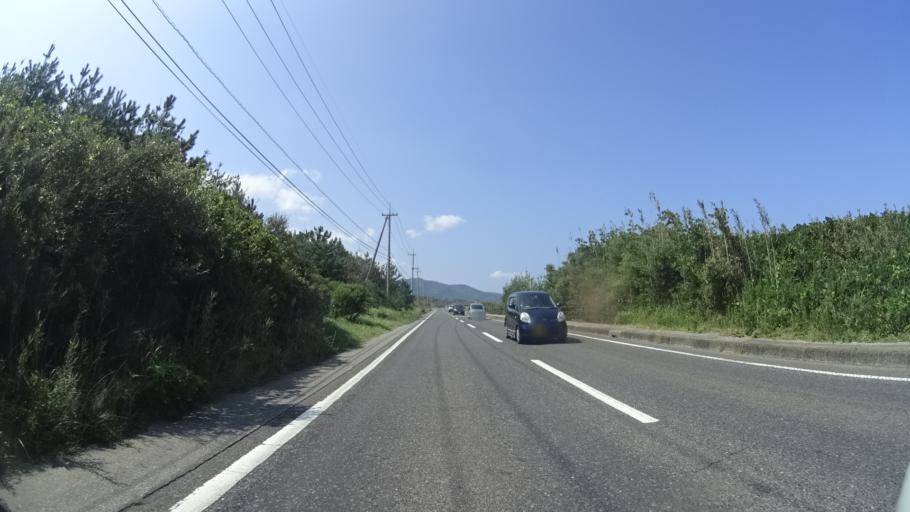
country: JP
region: Shimane
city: Masuda
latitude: 34.6794
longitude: 131.7650
